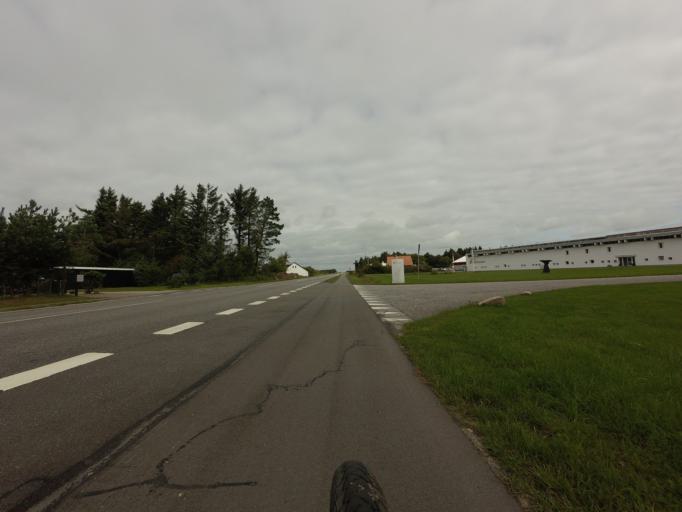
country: DK
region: North Denmark
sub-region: Hjorring Kommune
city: Hirtshals
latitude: 57.5759
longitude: 9.9443
